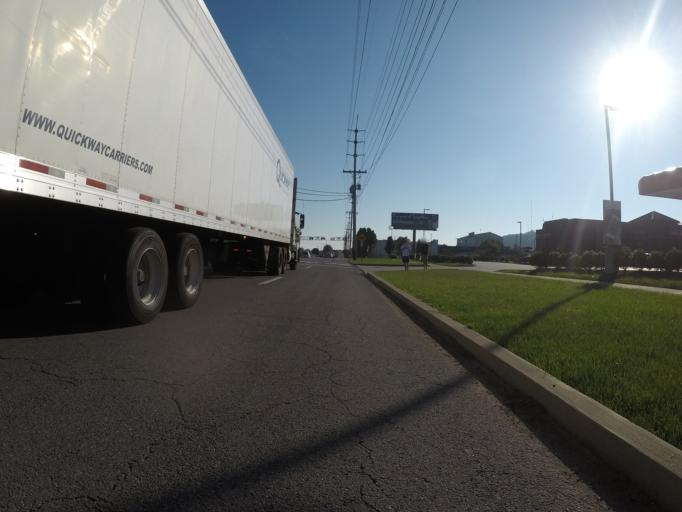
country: US
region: West Virginia
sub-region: Cabell County
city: Huntington
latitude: 38.4237
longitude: -82.4188
